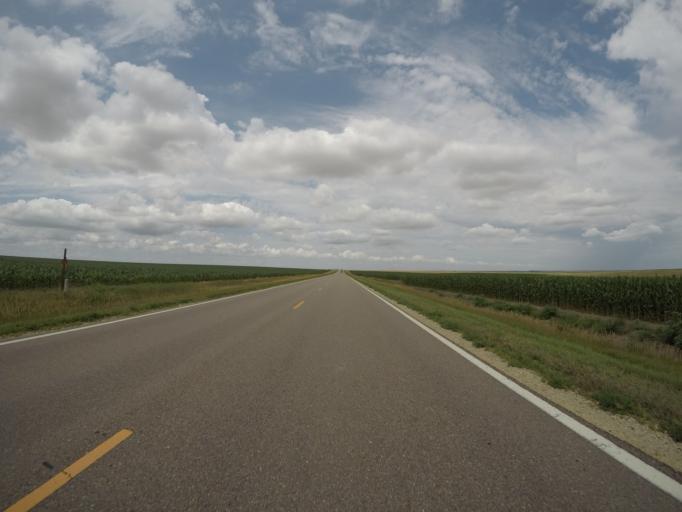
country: US
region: Kansas
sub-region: Rawlins County
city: Atwood
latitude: 39.6800
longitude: -101.0565
